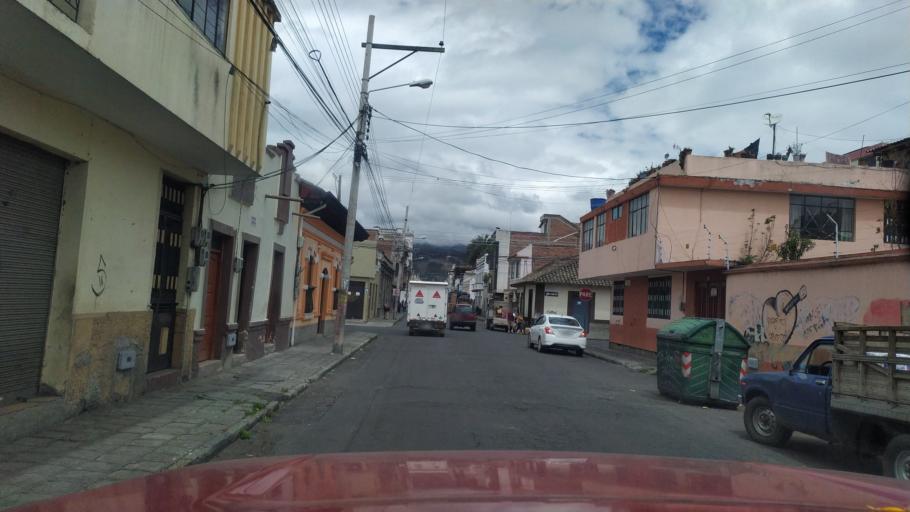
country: EC
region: Chimborazo
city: Riobamba
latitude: -1.6723
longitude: -78.6454
